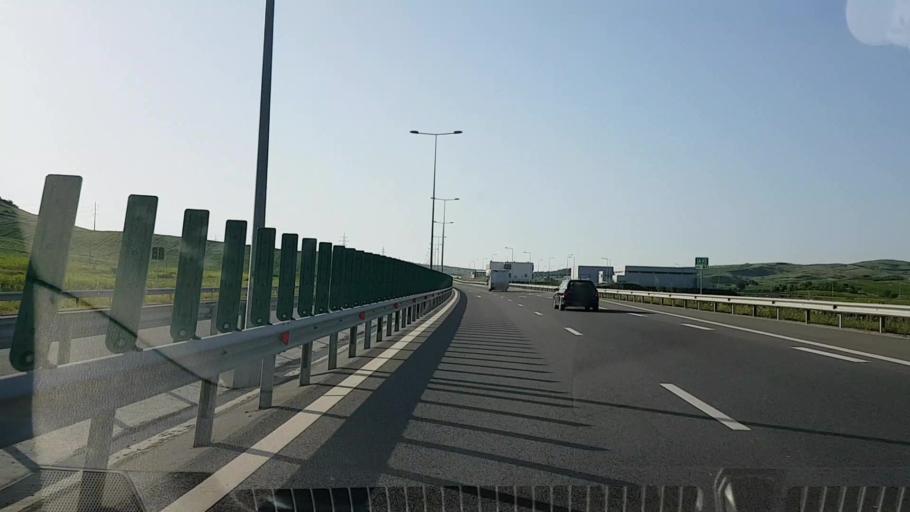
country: RO
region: Alba
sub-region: Comuna Unirea
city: Unirea
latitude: 46.4483
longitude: 23.7954
